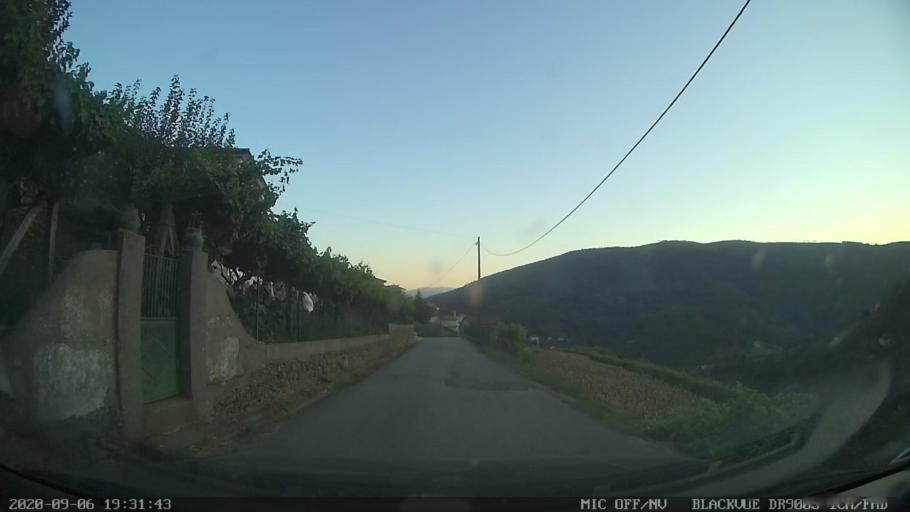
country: PT
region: Vila Real
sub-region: Mesao Frio
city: Mesao Frio
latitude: 41.1817
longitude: -7.9015
